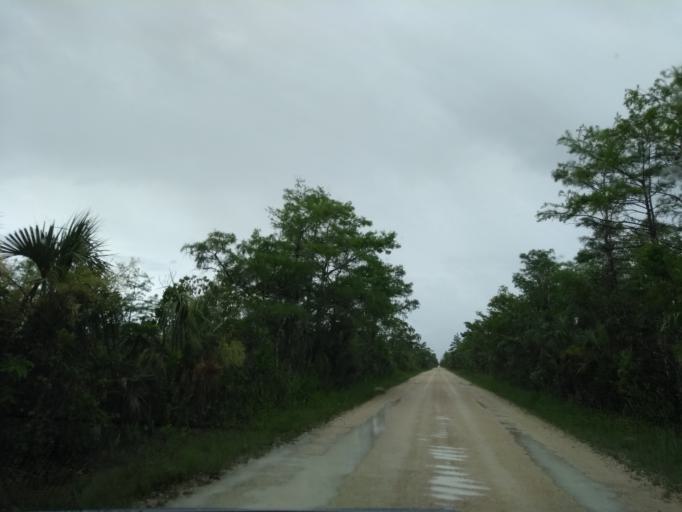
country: US
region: Florida
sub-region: Miami-Dade County
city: The Hammocks
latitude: 25.7602
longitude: -81.0194
